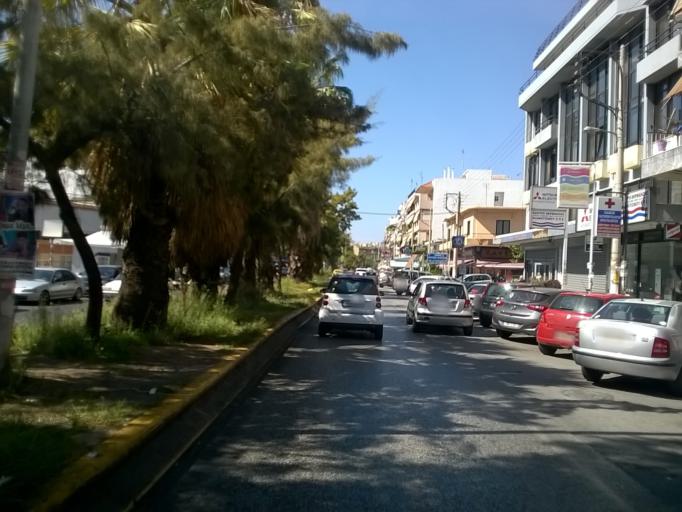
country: GR
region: Attica
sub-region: Nomos Piraios
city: Keratsini
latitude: 37.9642
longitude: 23.6326
